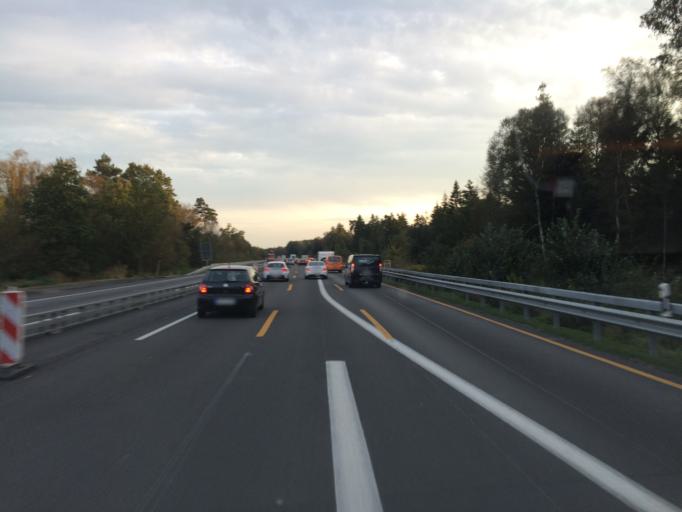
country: DE
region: Lower Saxony
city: Hademstorf
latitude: 52.7632
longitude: 9.6645
